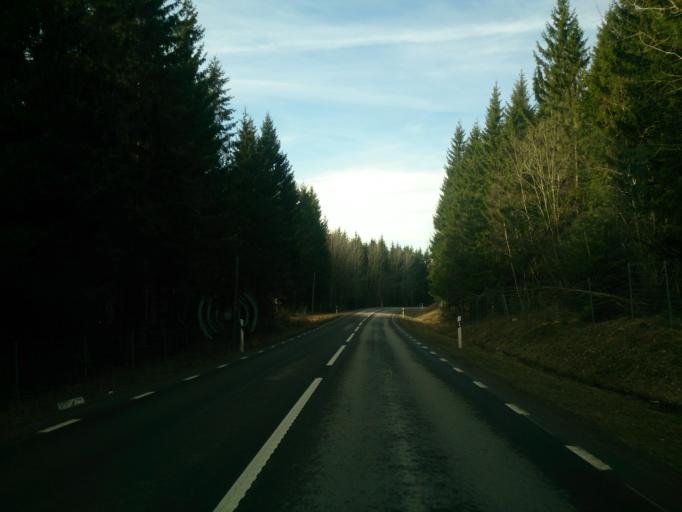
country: SE
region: OEstergoetland
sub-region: Atvidabergs Kommun
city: Atvidaberg
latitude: 58.1756
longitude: 16.0293
